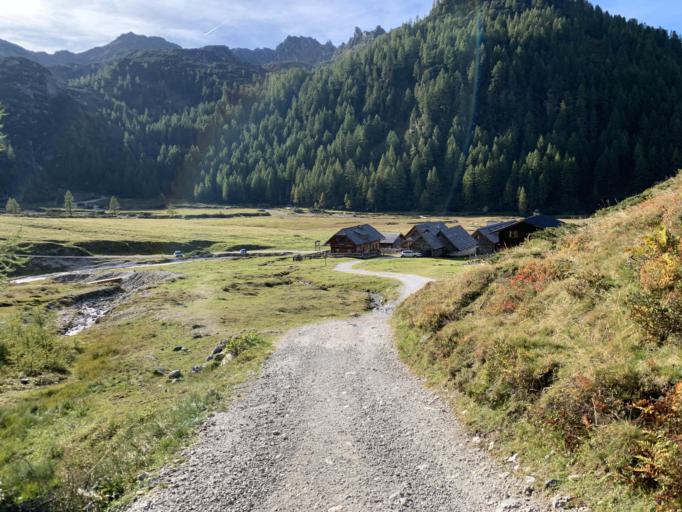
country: AT
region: Styria
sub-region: Politischer Bezirk Liezen
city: Schladming
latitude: 47.2962
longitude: 13.6257
